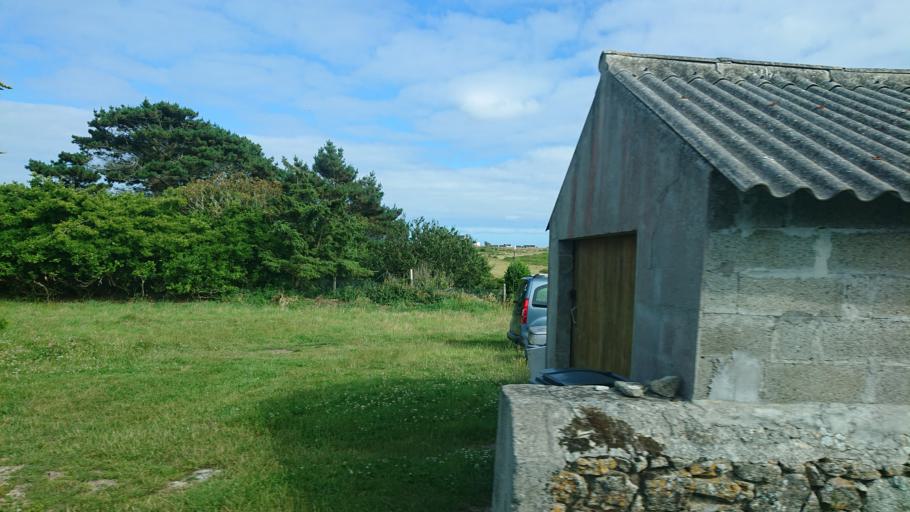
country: FR
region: Brittany
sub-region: Departement du Finistere
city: Porspoder
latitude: 48.4613
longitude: -5.0871
